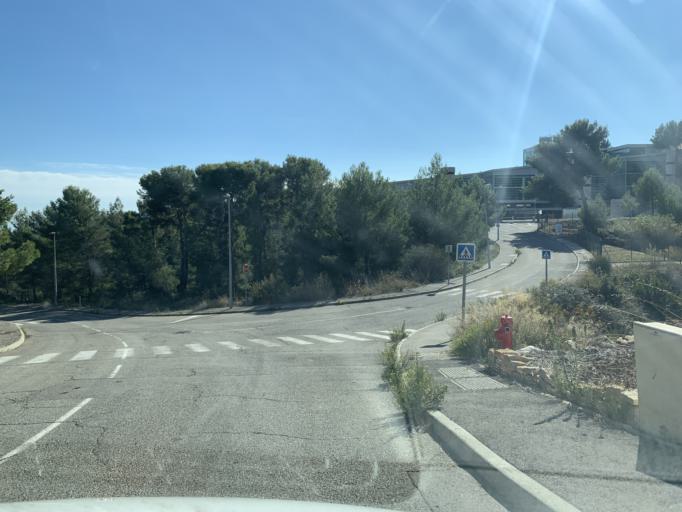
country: FR
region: Provence-Alpes-Cote d'Azur
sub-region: Departement des Bouches-du-Rhone
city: La Ciotat
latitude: 43.2077
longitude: 5.5971
